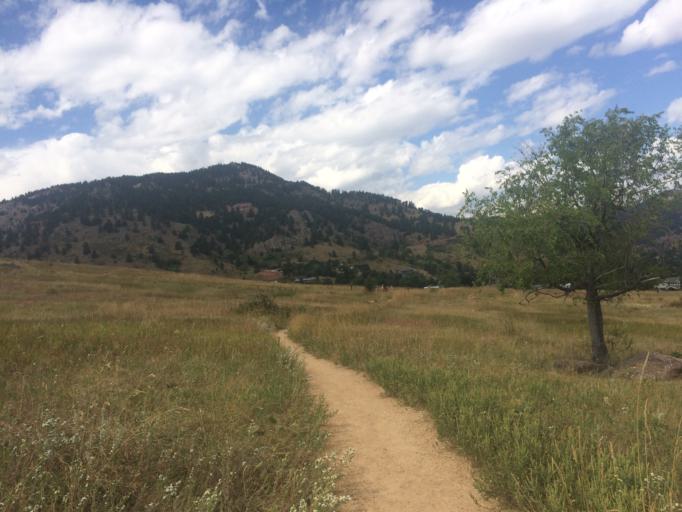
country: US
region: Colorado
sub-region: Boulder County
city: Boulder
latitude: 39.9977
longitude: -105.2833
